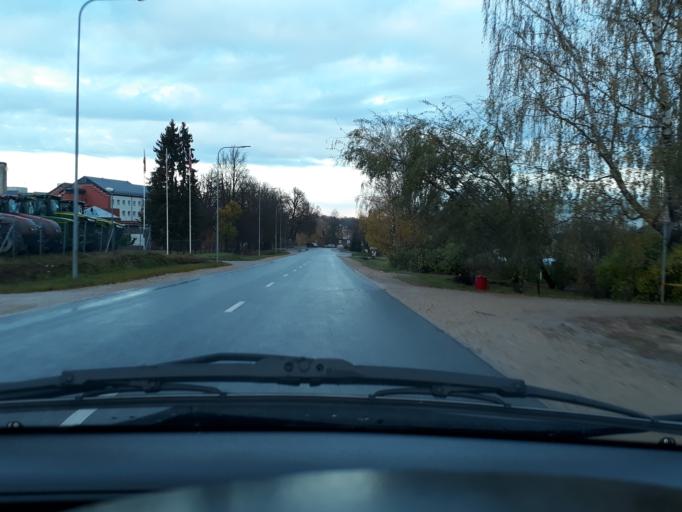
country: LV
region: Dobeles Rajons
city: Dobele
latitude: 56.6201
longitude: 23.2667
